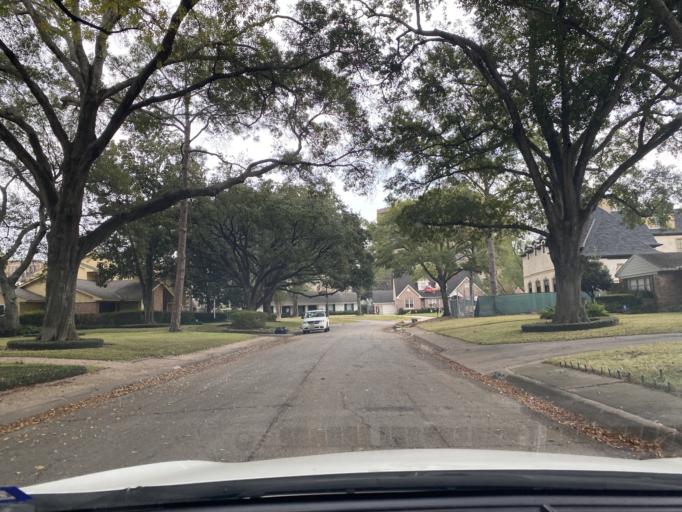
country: US
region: Texas
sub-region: Harris County
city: Hunters Creek Village
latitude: 29.7460
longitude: -95.4758
